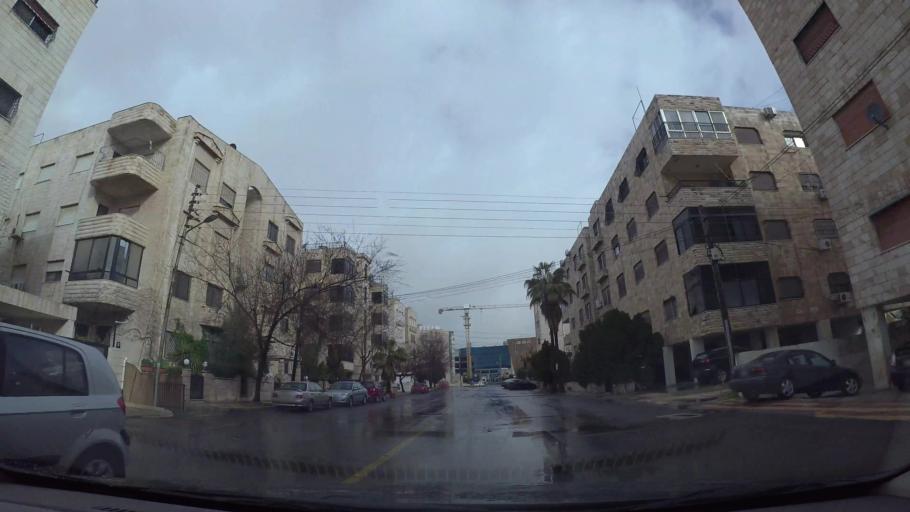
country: JO
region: Amman
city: Wadi as Sir
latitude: 31.9741
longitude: 35.8563
